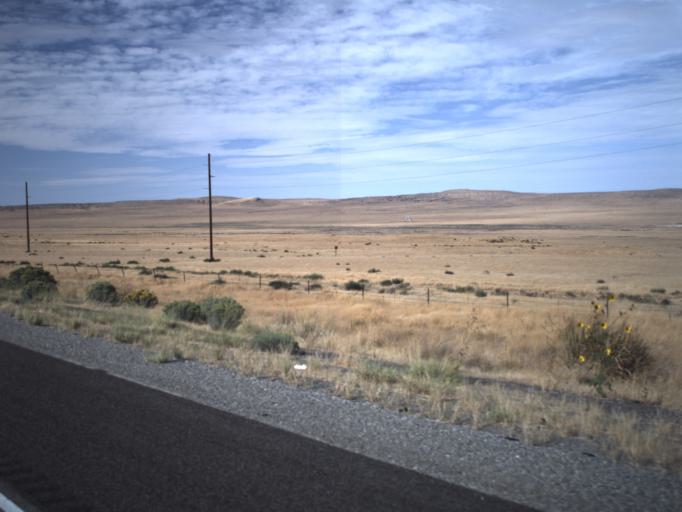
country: US
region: Utah
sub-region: Tooele County
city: Grantsville
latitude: 40.8016
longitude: -112.9416
